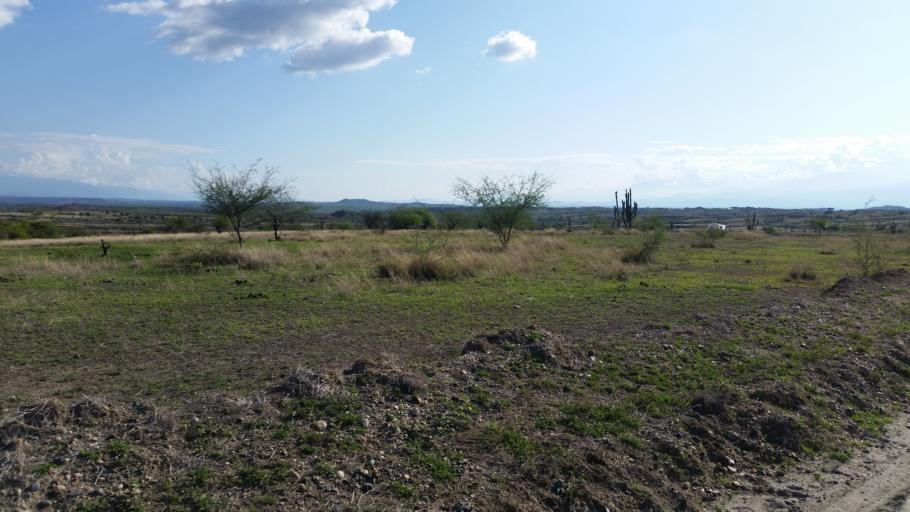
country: CO
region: Huila
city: Baraya
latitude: 3.2366
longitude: -75.1098
